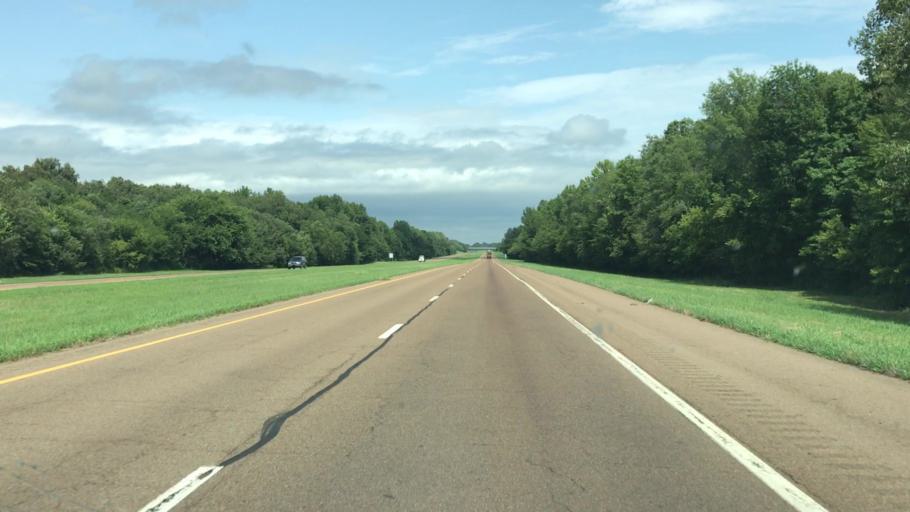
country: US
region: Tennessee
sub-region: Obion County
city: South Fulton
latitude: 36.4825
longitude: -88.9406
